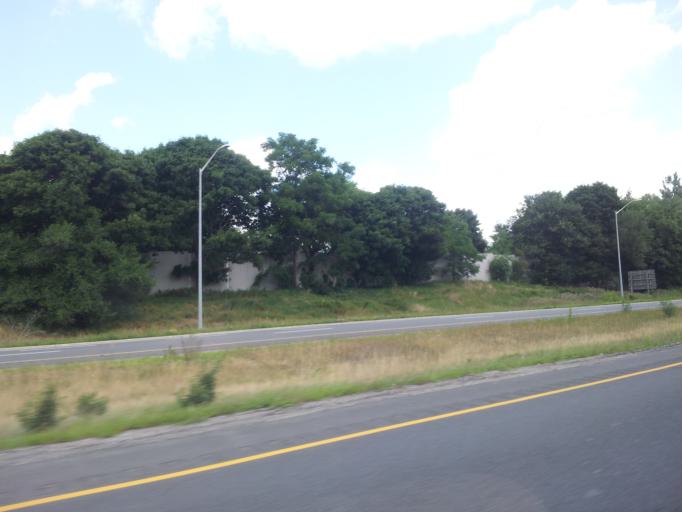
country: CA
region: Ontario
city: Waterloo
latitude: 43.4732
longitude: -80.4877
